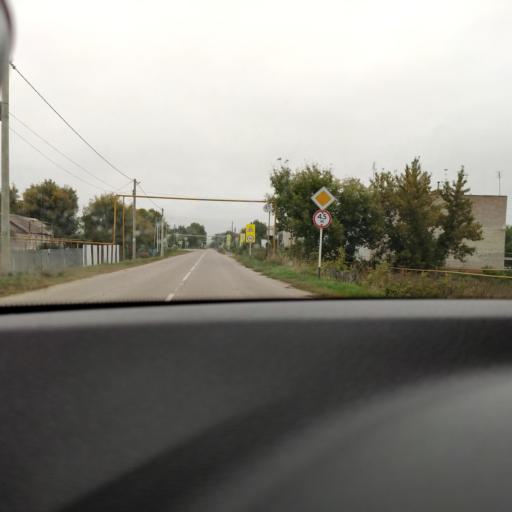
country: RU
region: Samara
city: Yelkhovka
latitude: 53.7361
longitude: 50.3192
